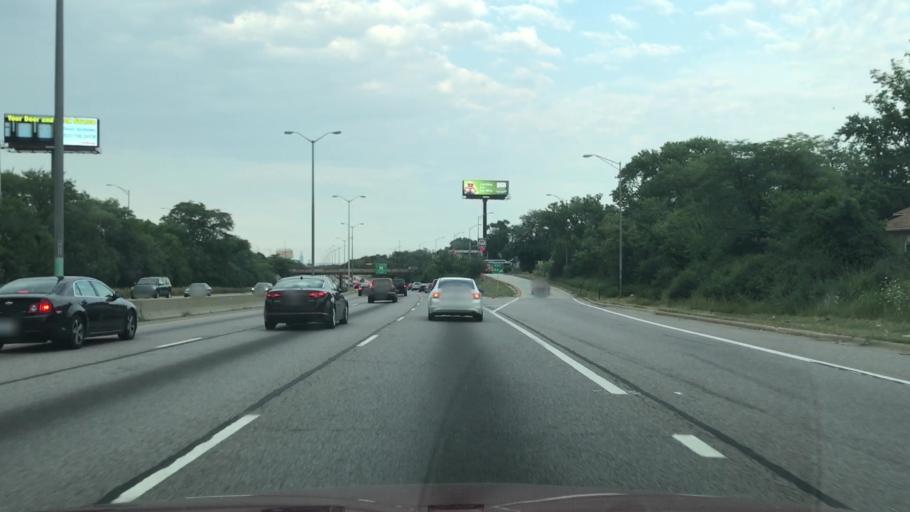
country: US
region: Illinois
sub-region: Cook County
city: Broadview
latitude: 41.8709
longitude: -87.8568
